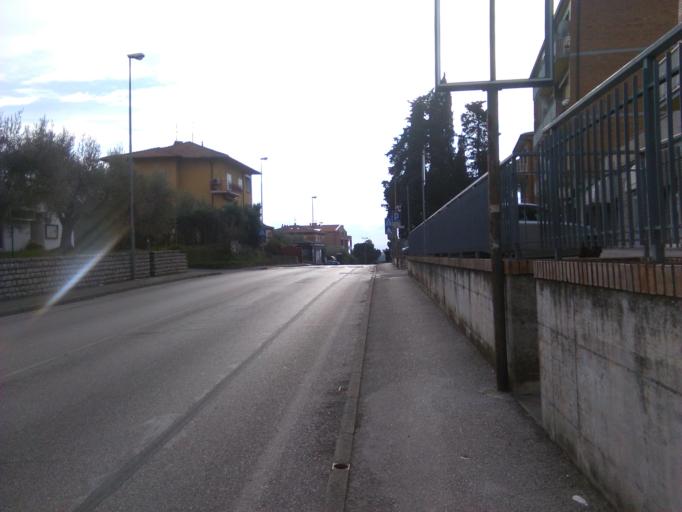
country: IT
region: Umbria
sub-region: Provincia di Perugia
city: Perugia
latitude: 43.0980
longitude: 12.3644
